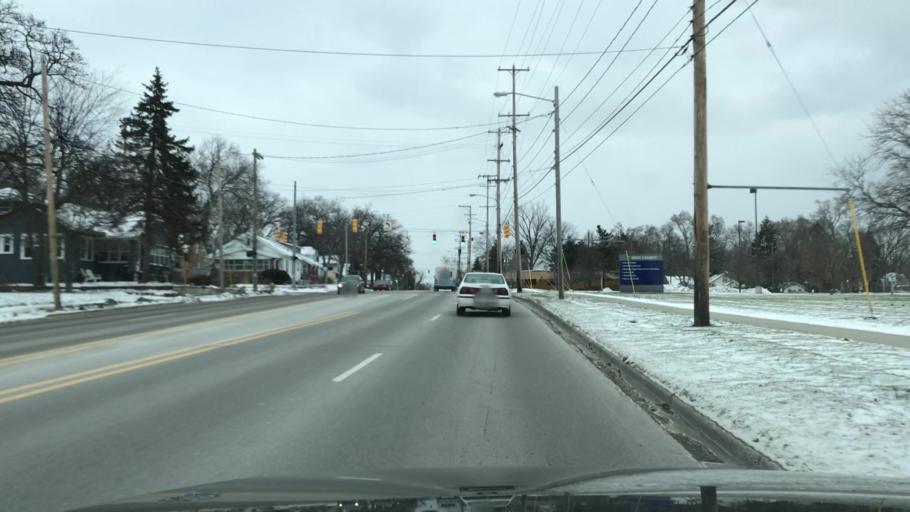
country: US
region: Michigan
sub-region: Kent County
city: Grand Rapids
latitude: 42.9757
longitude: -85.6397
